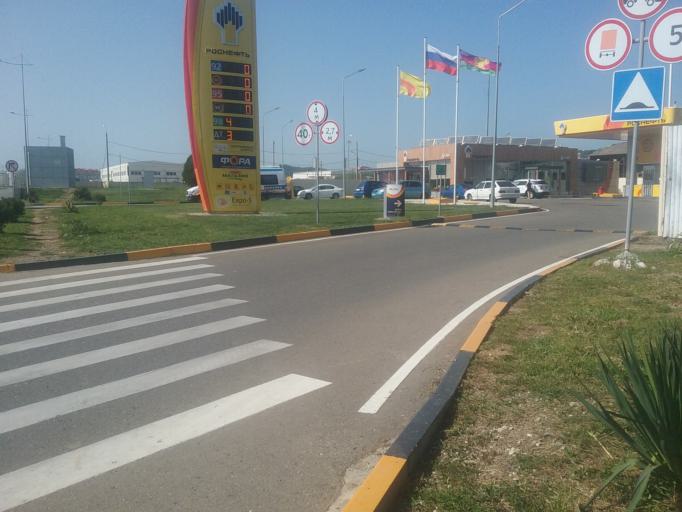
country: RU
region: Krasnodarskiy
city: Vysokoye
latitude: 43.3959
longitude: 39.9888
